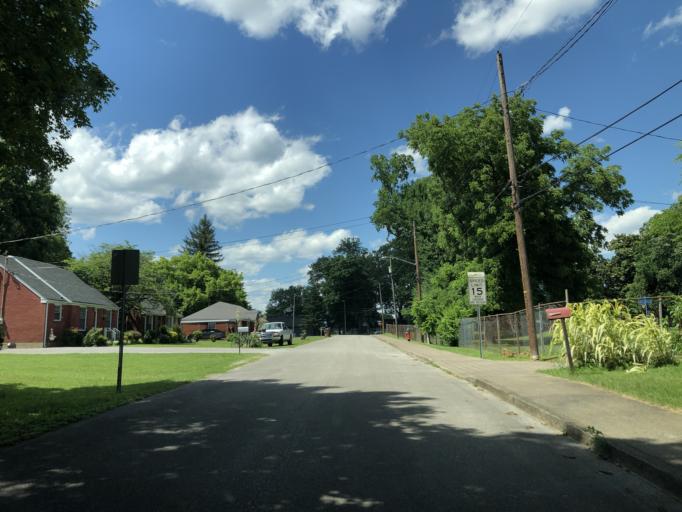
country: US
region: Tennessee
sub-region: Davidson County
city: Nashville
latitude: 36.1881
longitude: -86.7364
